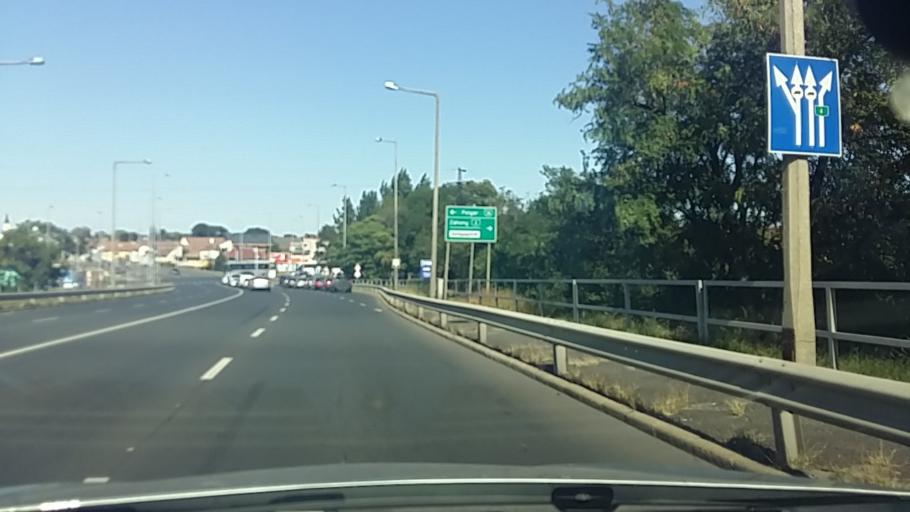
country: HU
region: Szabolcs-Szatmar-Bereg
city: Nyiregyhaza
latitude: 47.9412
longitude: 21.7197
